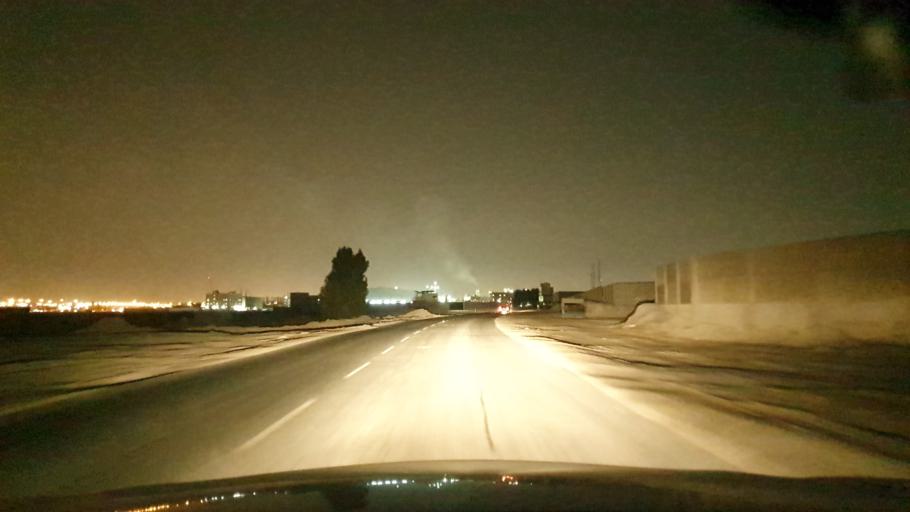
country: BH
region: Northern
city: Sitrah
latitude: 26.0886
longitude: 50.6166
